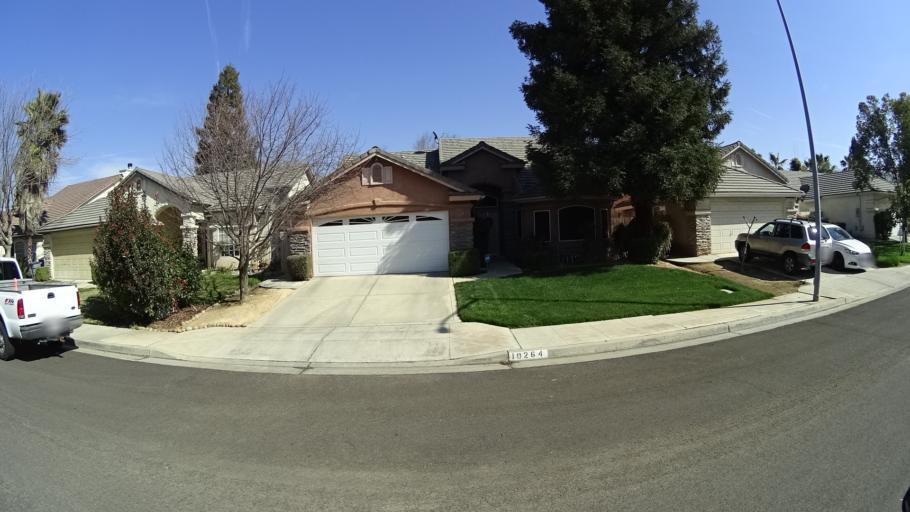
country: US
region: California
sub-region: Fresno County
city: Clovis
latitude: 36.8850
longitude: -119.7411
